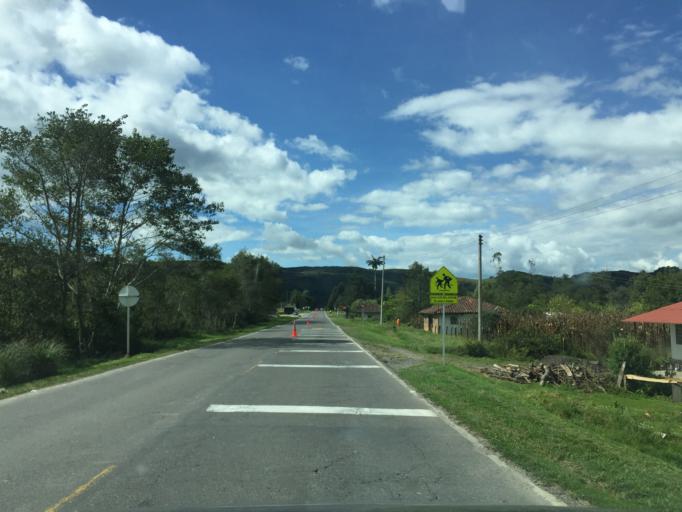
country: CO
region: Boyaca
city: Arcabuco
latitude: 5.7824
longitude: -73.4615
